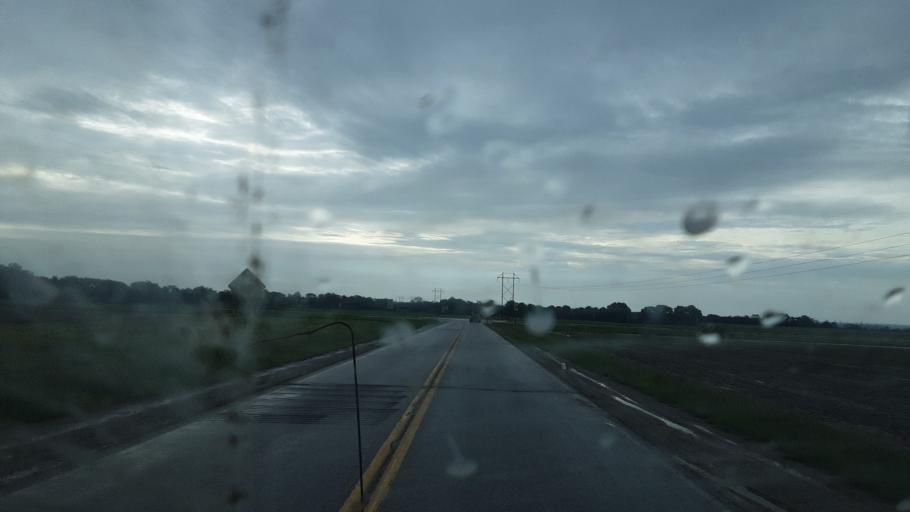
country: US
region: Missouri
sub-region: Clark County
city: Kahoka
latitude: 40.4305
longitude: -91.5731
